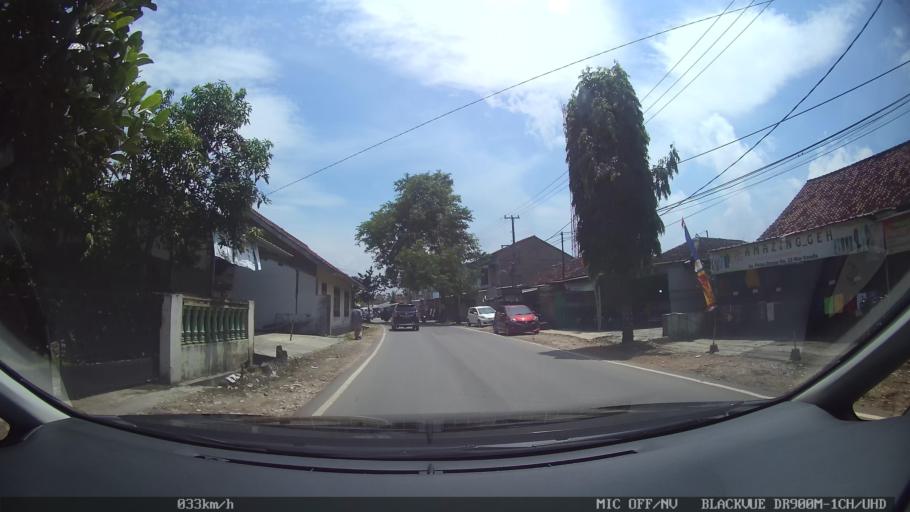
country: ID
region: Lampung
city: Kedaton
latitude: -5.3569
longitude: 105.2885
